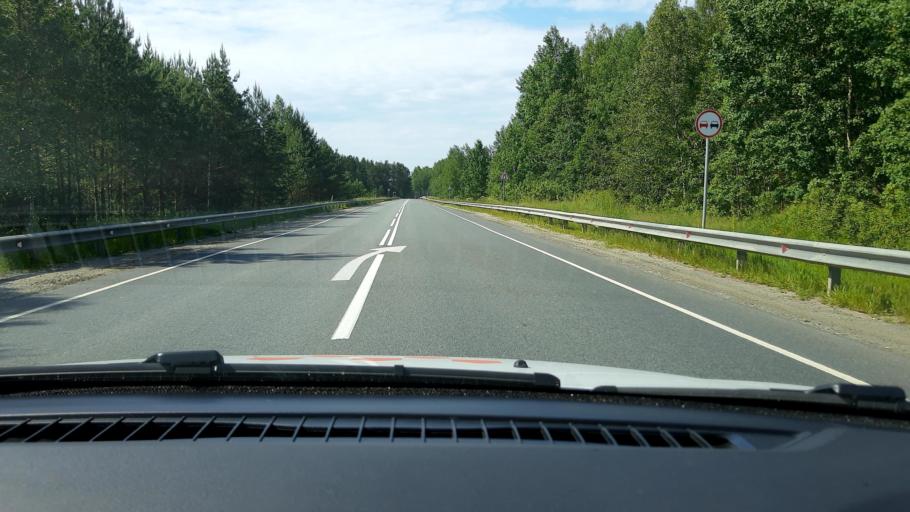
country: RU
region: Nizjnij Novgorod
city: Linda
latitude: 56.6632
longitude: 44.1308
